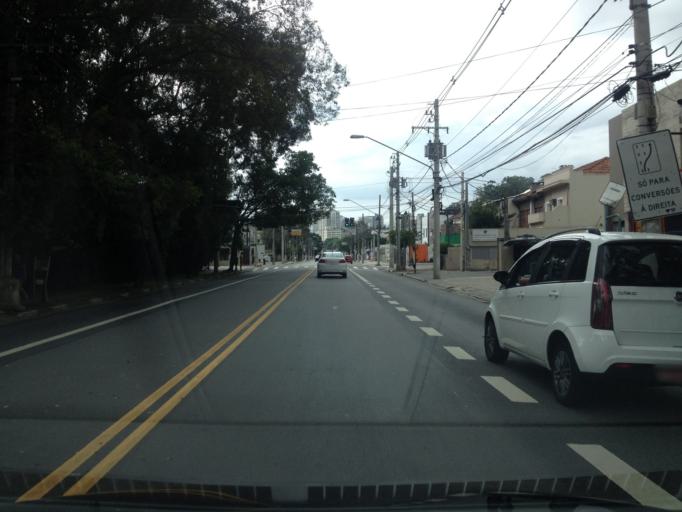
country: BR
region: Sao Paulo
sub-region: Sao Paulo
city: Sao Paulo
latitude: -23.5819
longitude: -46.6663
